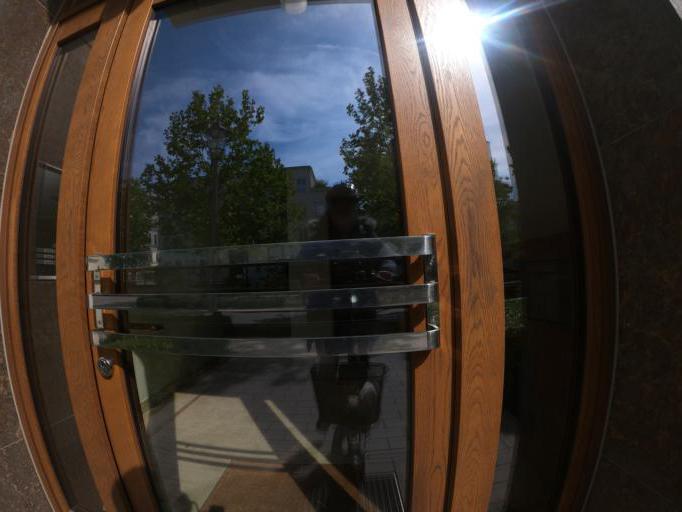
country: DE
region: North Rhine-Westphalia
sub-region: Regierungsbezirk Dusseldorf
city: Dusseldorf
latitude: 51.2384
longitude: 6.7302
